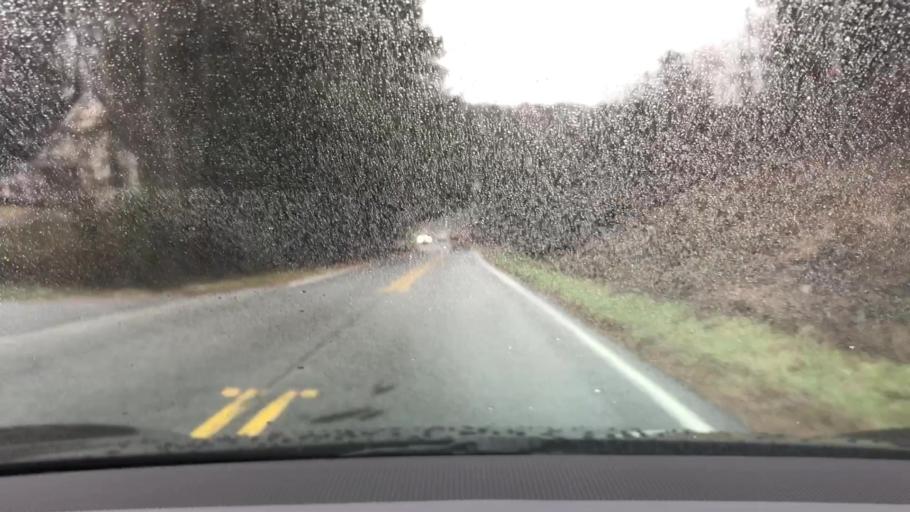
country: US
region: Georgia
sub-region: Forsyth County
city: Cumming
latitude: 34.1931
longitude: -84.1221
